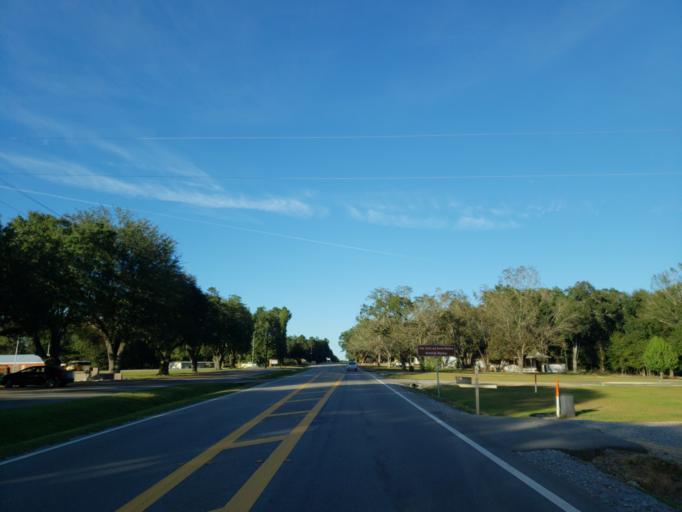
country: US
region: Mississippi
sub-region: Perry County
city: Richton
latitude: 31.3491
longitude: -88.7619
